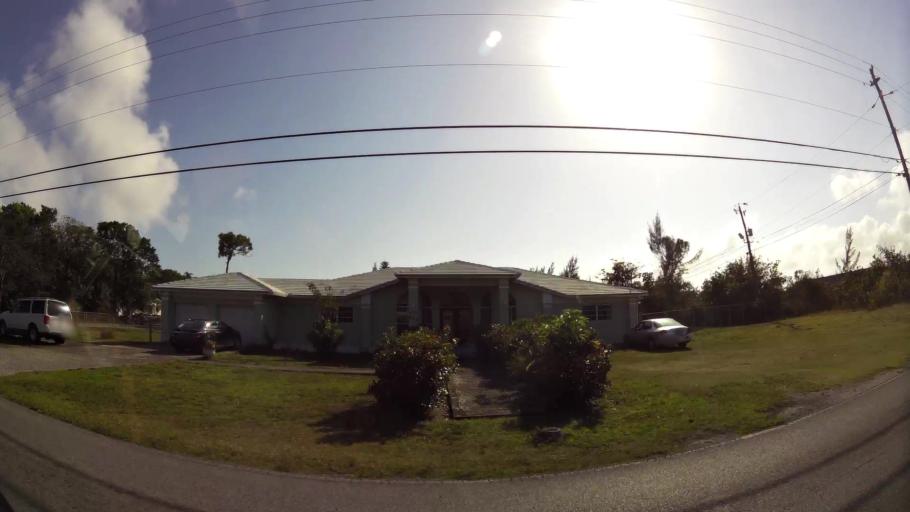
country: BS
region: Freeport
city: Lucaya
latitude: 26.5122
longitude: -78.6620
